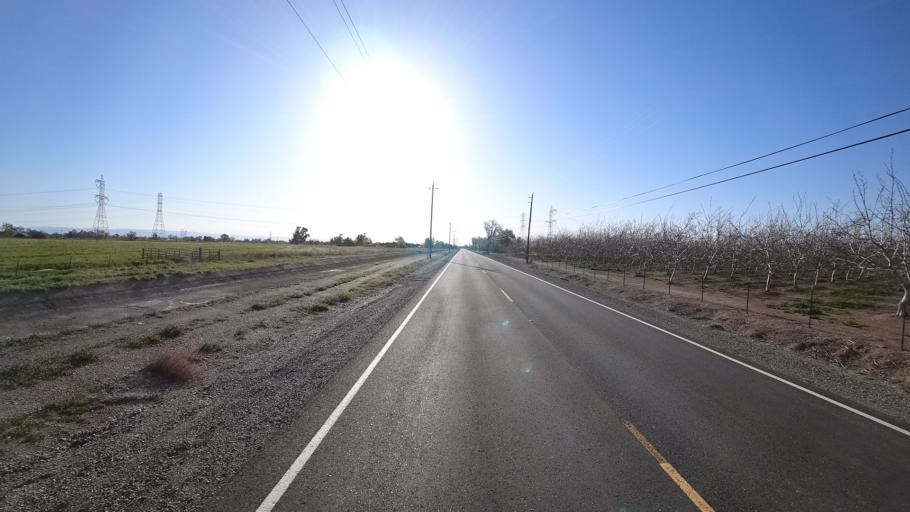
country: US
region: California
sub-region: Glenn County
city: Orland
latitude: 39.7768
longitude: -122.2777
